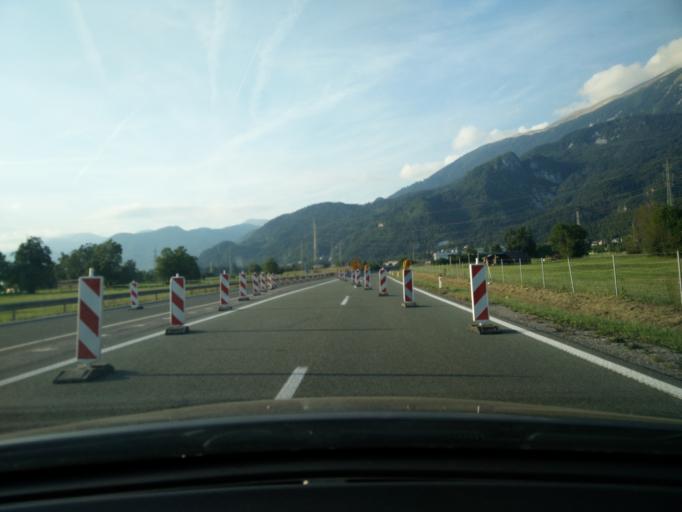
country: SI
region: Zirovnica
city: Zirovnica
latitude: 46.3971
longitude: 14.1327
